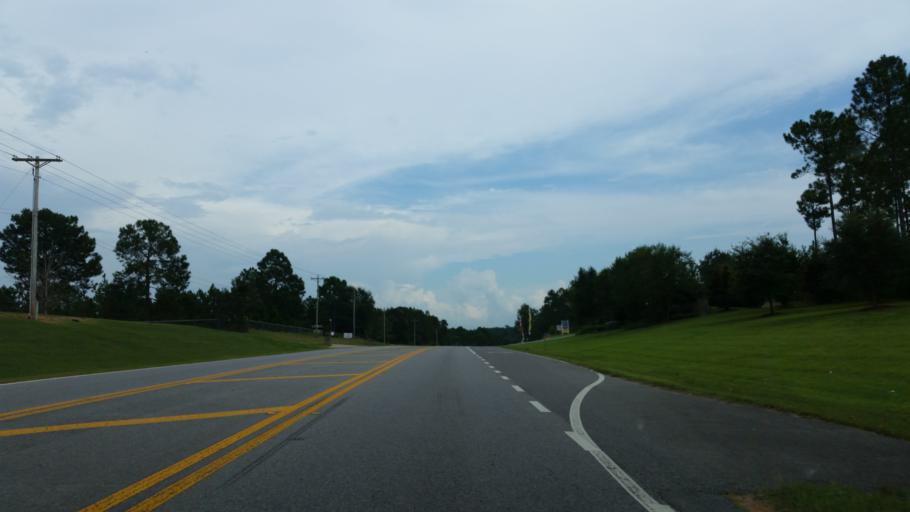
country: US
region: Florida
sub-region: Santa Rosa County
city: Wallace
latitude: 30.6714
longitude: -87.2184
